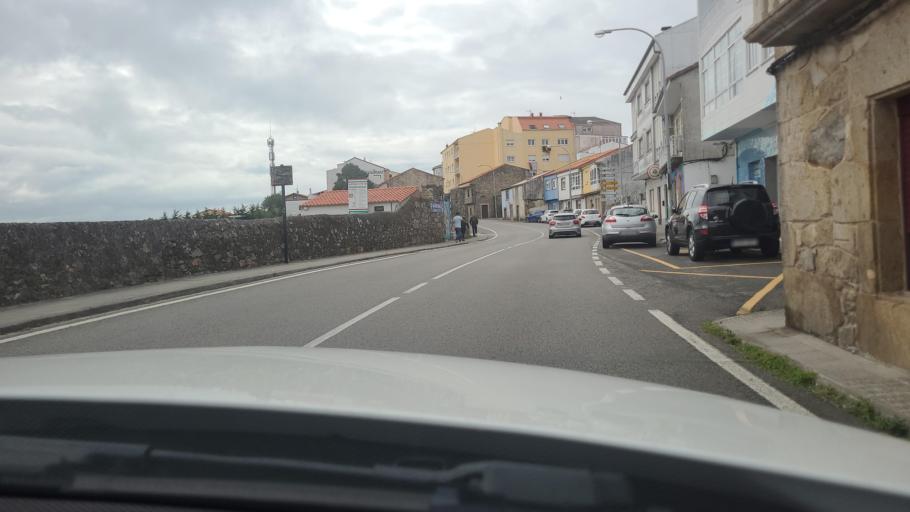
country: ES
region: Galicia
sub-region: Provincia da Coruna
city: Fisterra
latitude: 42.9116
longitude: -9.2638
